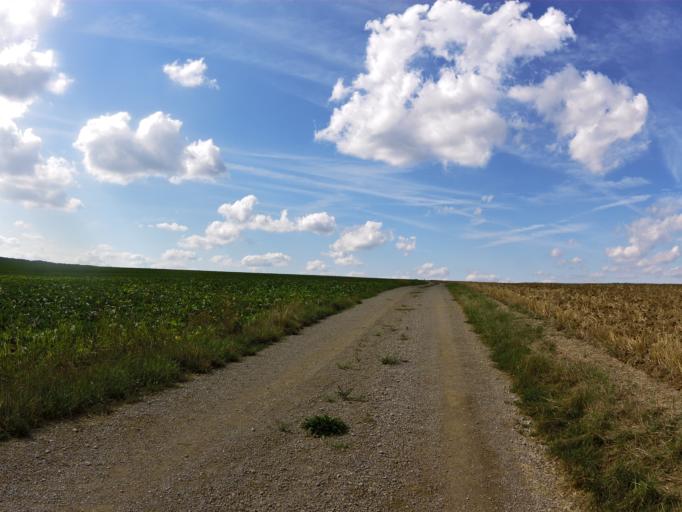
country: DE
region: Bavaria
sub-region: Regierungsbezirk Unterfranken
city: Reichenberg
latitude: 49.7174
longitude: 9.9141
